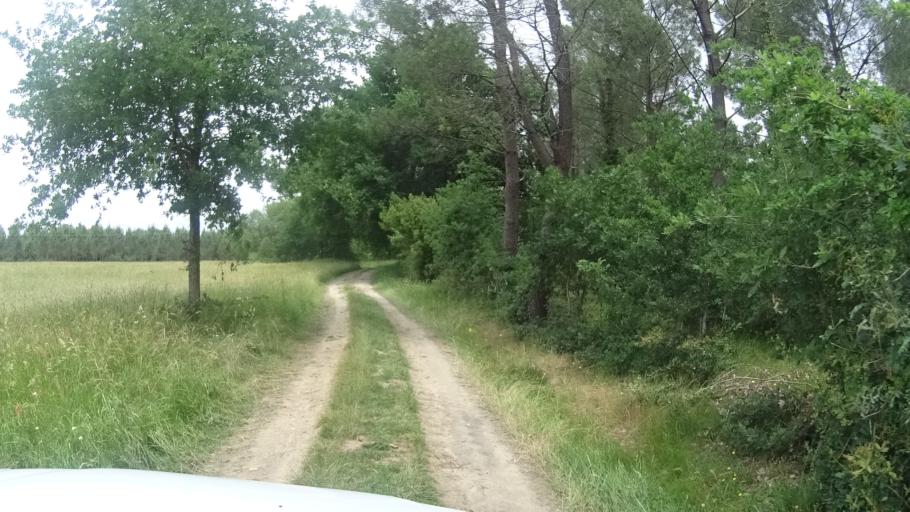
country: FR
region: Aquitaine
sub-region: Departement de la Dordogne
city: Riberac
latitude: 45.1528
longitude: 0.2709
